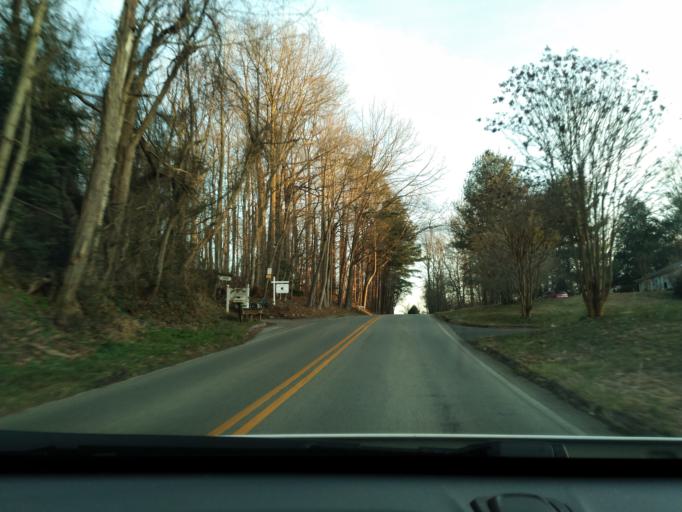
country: US
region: Maryland
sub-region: Calvert County
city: Huntingtown
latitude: 38.5927
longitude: -76.5608
